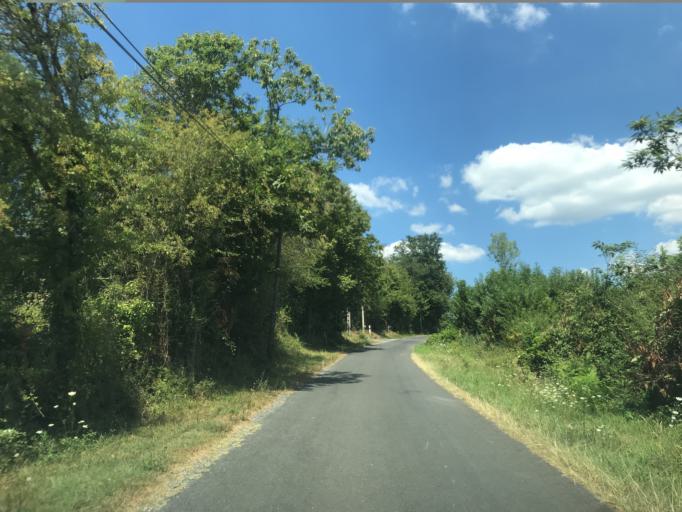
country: FR
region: Aquitaine
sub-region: Departement de la Dordogne
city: Cenac-et-Saint-Julien
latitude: 44.8339
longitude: 1.1920
